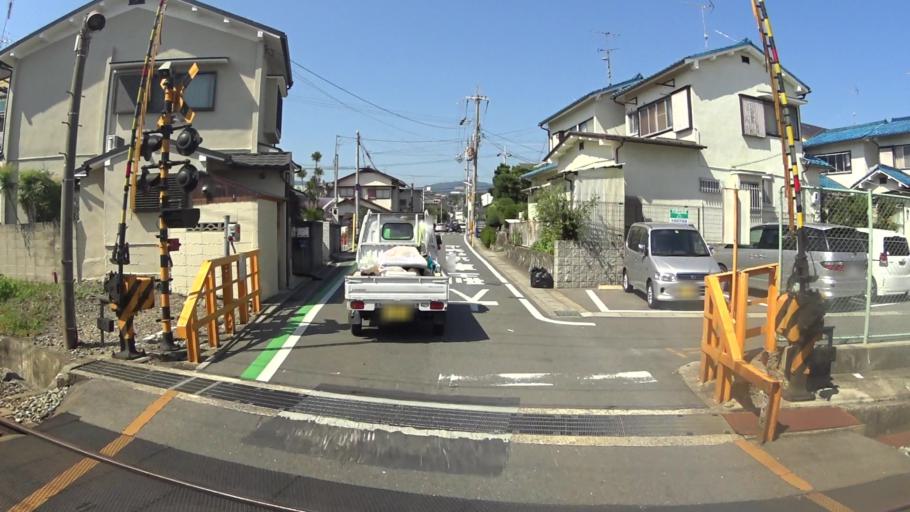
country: JP
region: Kyoto
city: Muko
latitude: 34.9425
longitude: 135.7045
